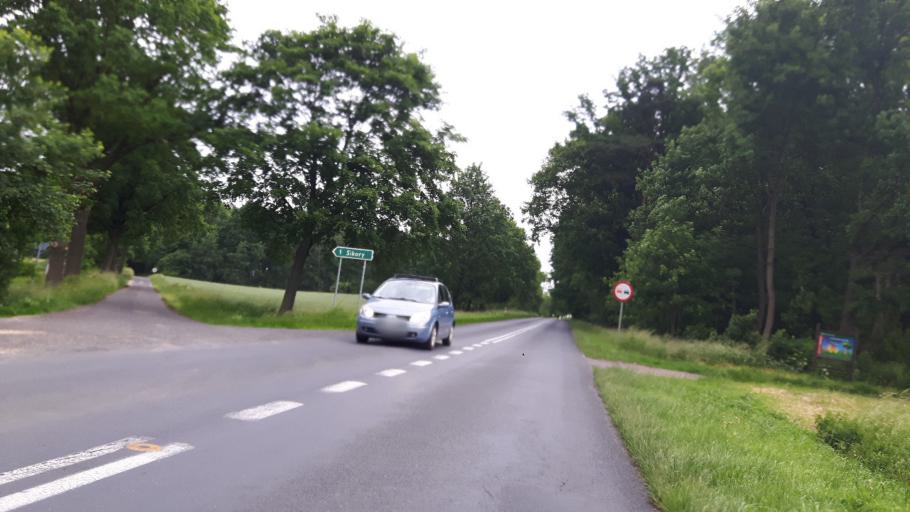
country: PL
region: West Pomeranian Voivodeship
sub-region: Powiat gryficki
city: Gryfice
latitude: 53.9435
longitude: 15.2215
